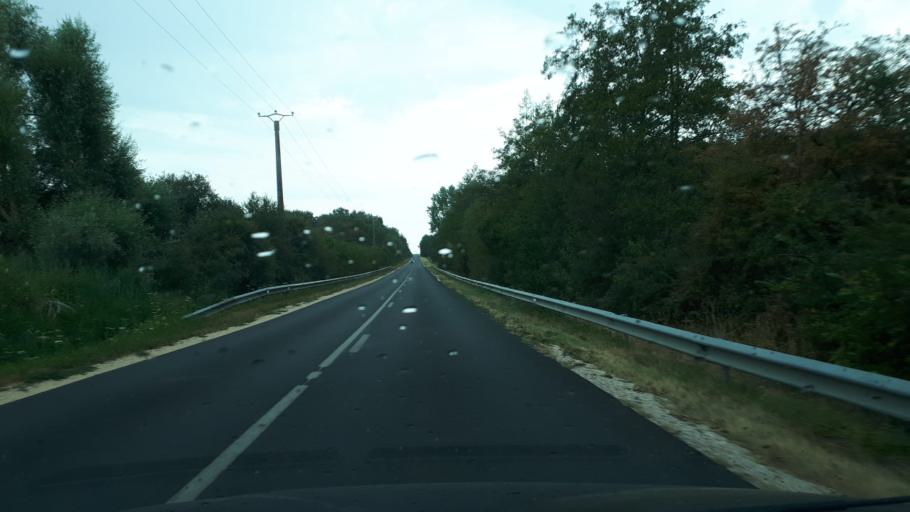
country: FR
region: Centre
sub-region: Departement du Loir-et-Cher
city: Saint-Romain-sur-Cher
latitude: 47.3499
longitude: 1.4029
